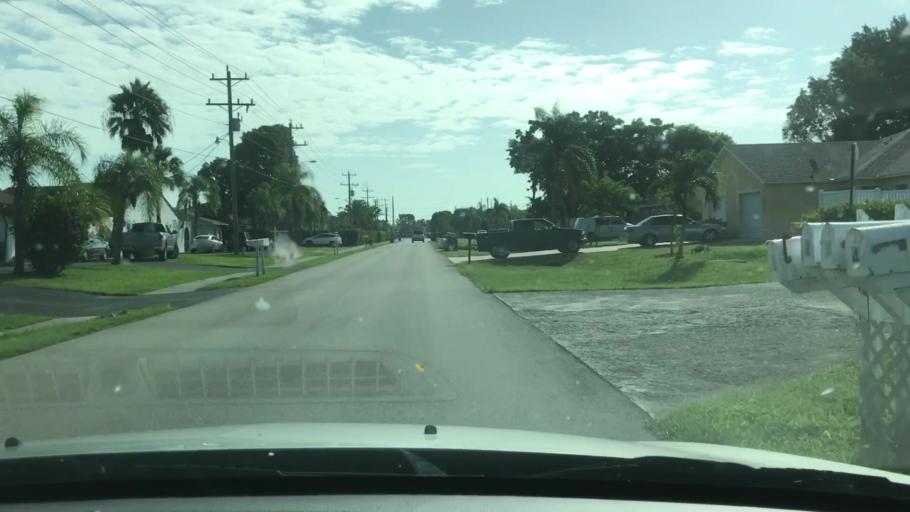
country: US
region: Florida
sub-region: Lee County
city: Lochmoor Waterway Estates
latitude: 26.6379
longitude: -81.9483
